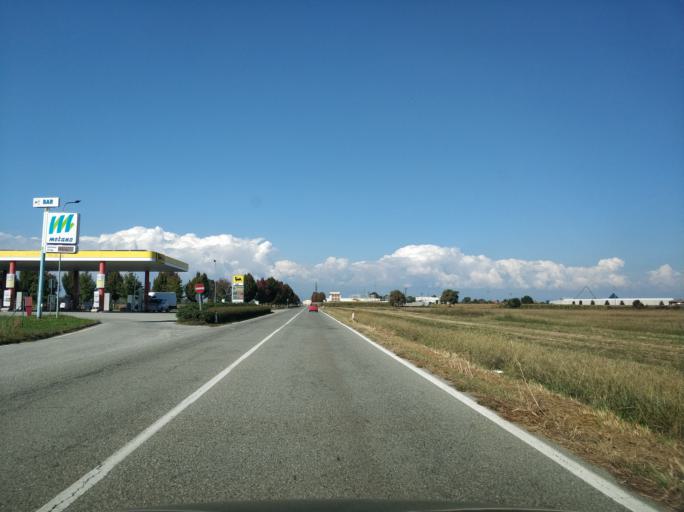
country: IT
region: Piedmont
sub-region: Provincia di Torino
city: Borgaro Torinese
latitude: 45.1458
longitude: 7.6782
